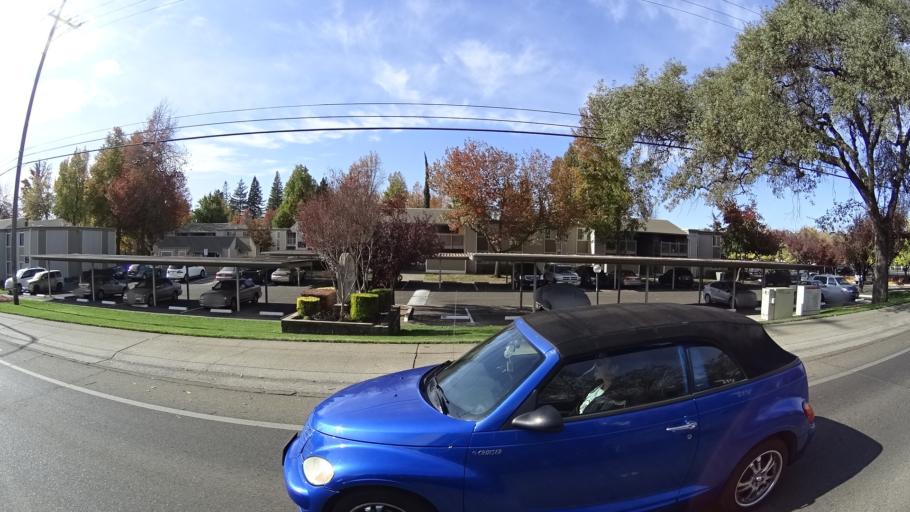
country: US
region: California
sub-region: Sacramento County
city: Fair Oaks
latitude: 38.6734
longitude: -121.2622
